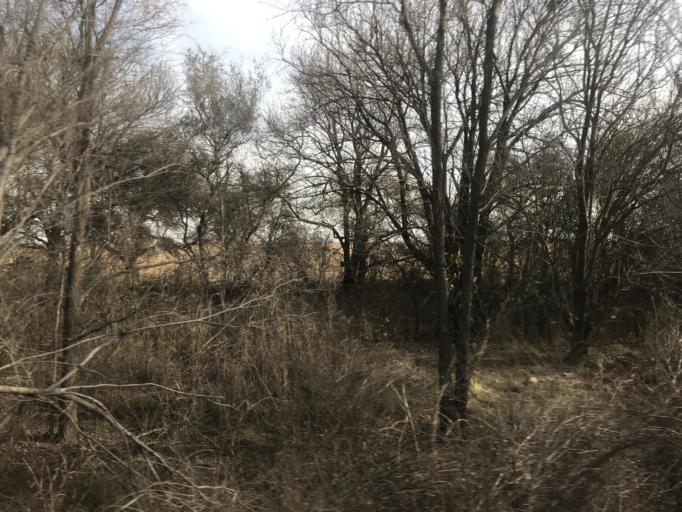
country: AR
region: Cordoba
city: Pilar
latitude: -31.7193
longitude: -63.8533
